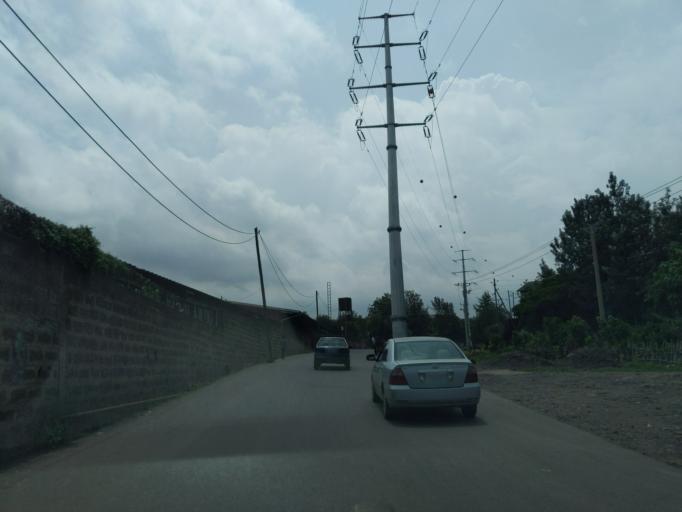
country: ET
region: Adis Abeba
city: Addis Ababa
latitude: 8.9560
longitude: 38.7607
